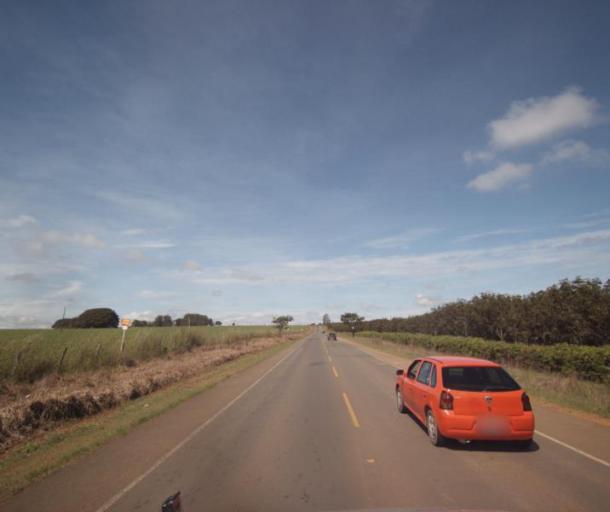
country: BR
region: Goias
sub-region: Anapolis
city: Anapolis
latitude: -16.1867
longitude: -48.9042
